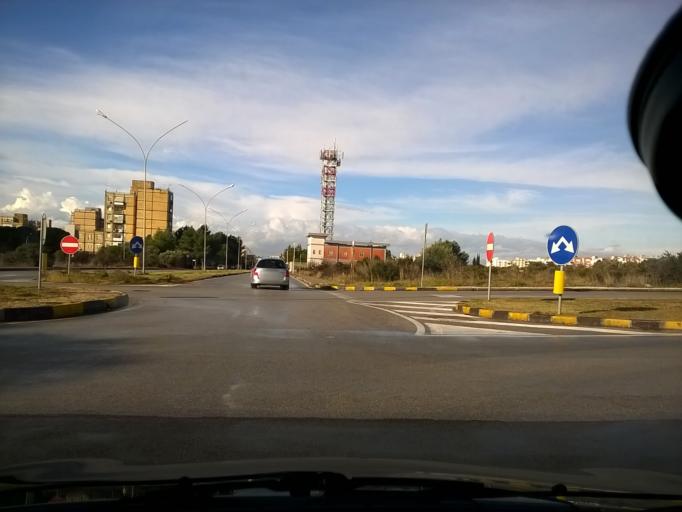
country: IT
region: Apulia
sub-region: Provincia di Taranto
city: Paolo VI
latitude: 40.5238
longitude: 17.2814
